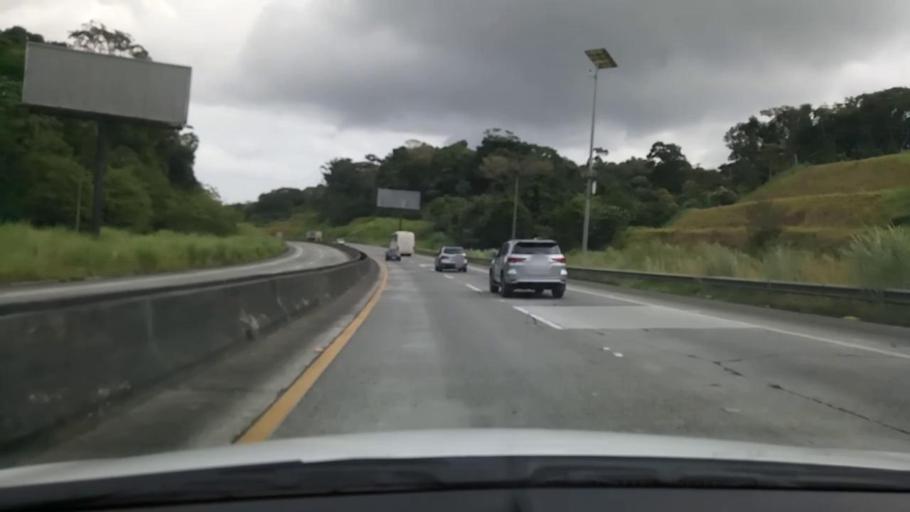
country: PA
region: Colon
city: Gatun
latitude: 9.2844
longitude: -79.7773
